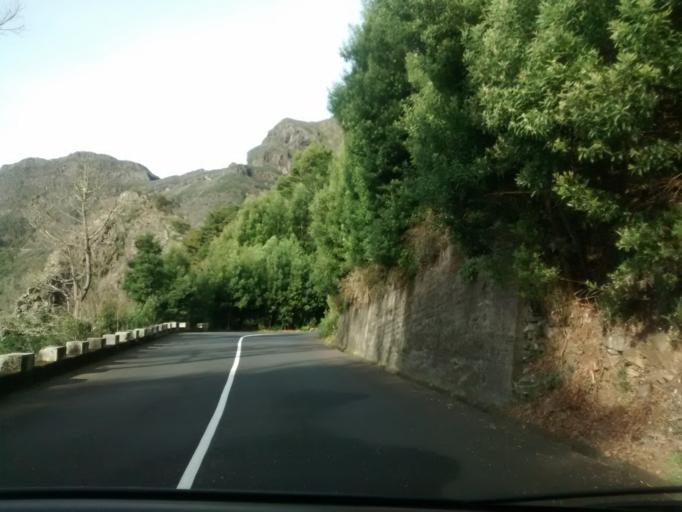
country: PT
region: Madeira
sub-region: Sao Vicente
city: Sao Vicente
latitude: 32.7533
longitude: -17.0210
